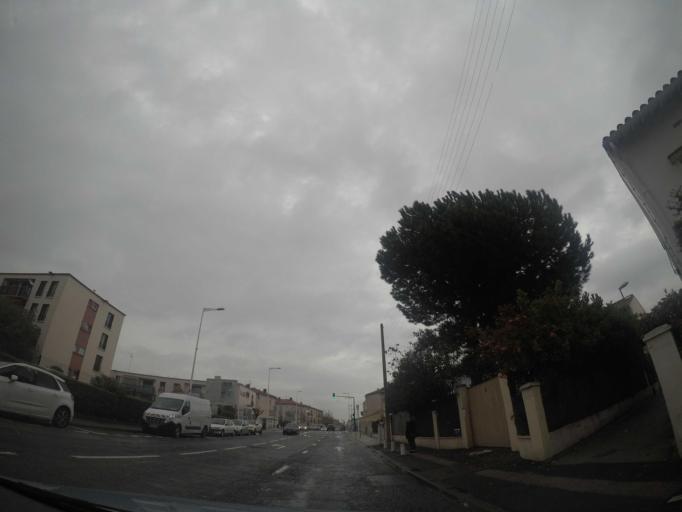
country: FR
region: Languedoc-Roussillon
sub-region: Departement des Pyrenees-Orientales
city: Perpignan
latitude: 42.6936
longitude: 2.8725
